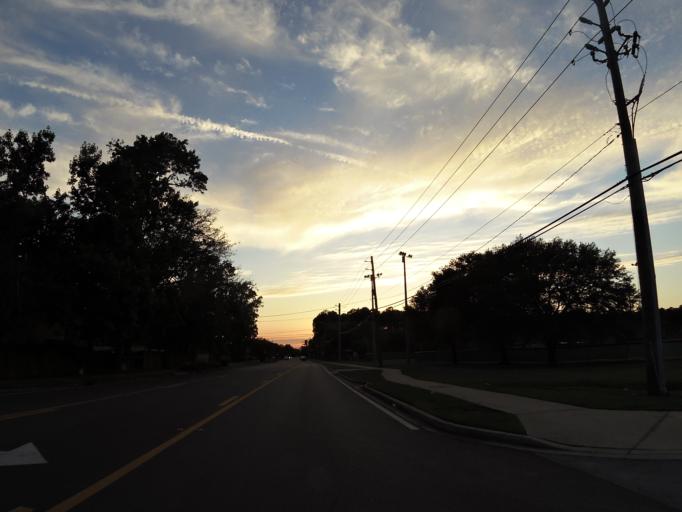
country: US
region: Florida
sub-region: Duval County
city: Jacksonville
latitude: 30.2702
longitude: -81.5965
